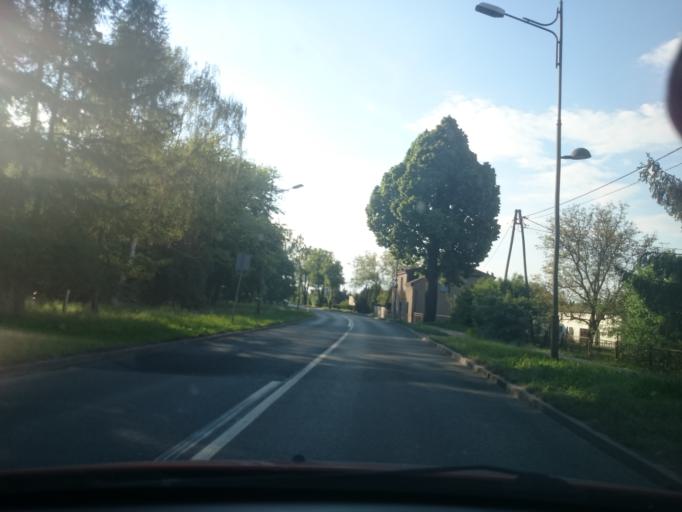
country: PL
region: Opole Voivodeship
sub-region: Powiat strzelecki
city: Strzelce Opolskie
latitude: 50.5183
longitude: 18.2865
